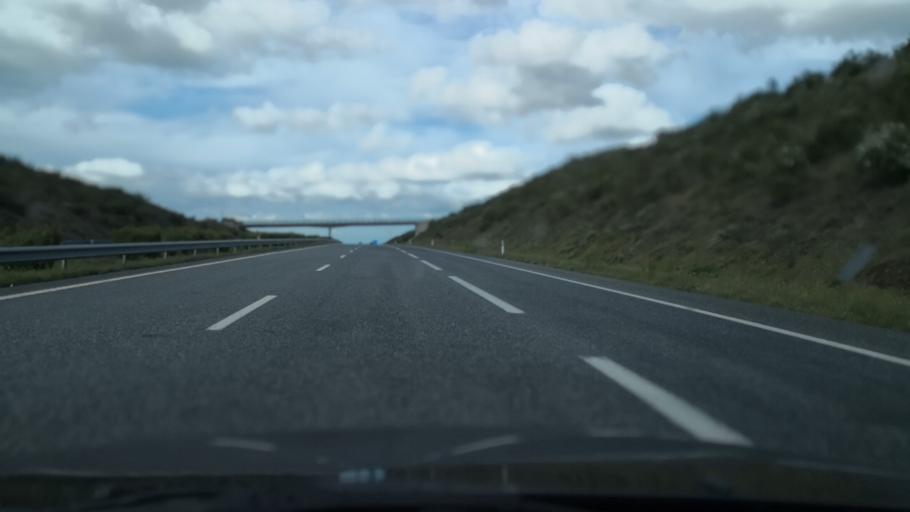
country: PT
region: Evora
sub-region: Estremoz
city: Estremoz
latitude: 38.7595
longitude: -7.7086
